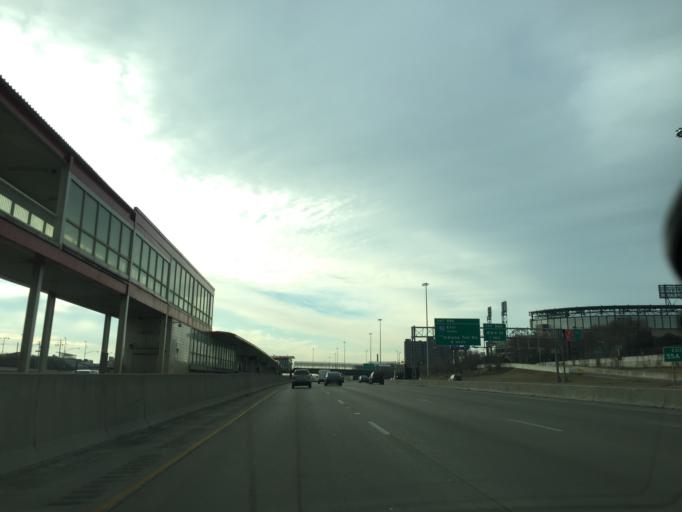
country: US
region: Illinois
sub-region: Cook County
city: Chicago
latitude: 41.8338
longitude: -87.6308
